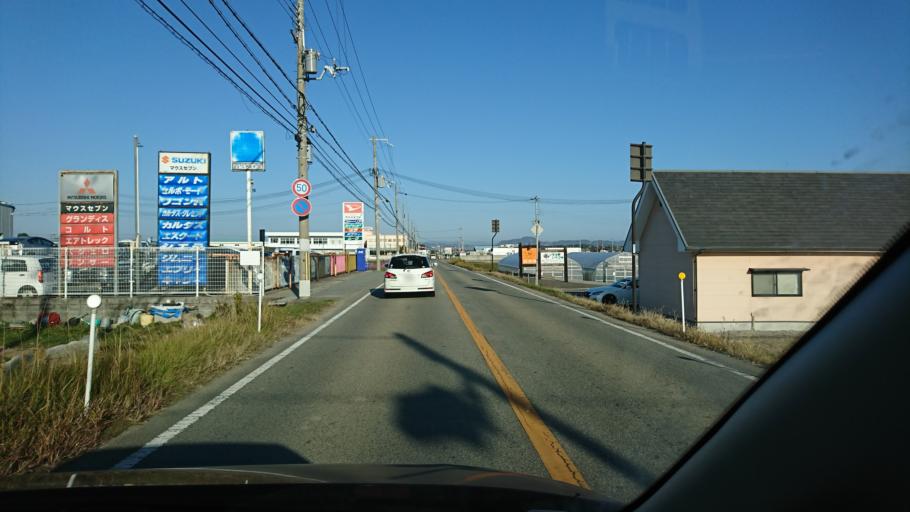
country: JP
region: Hyogo
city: Kakogawacho-honmachi
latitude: 34.7510
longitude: 134.8945
